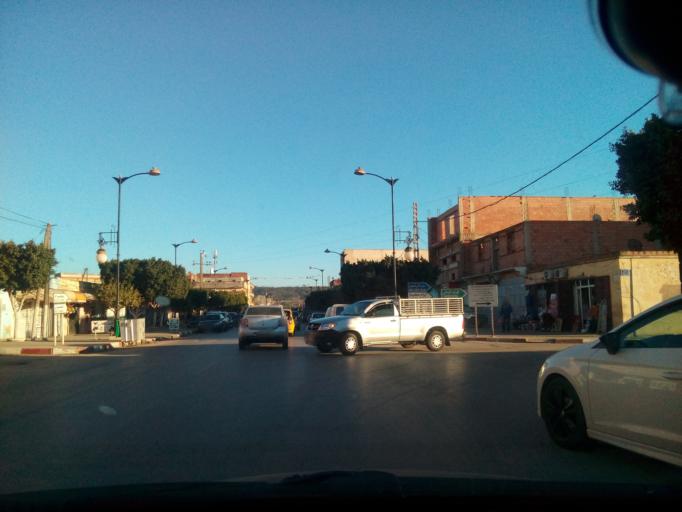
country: DZ
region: Mostaganem
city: Mostaganem
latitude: 35.7819
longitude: 0.1852
